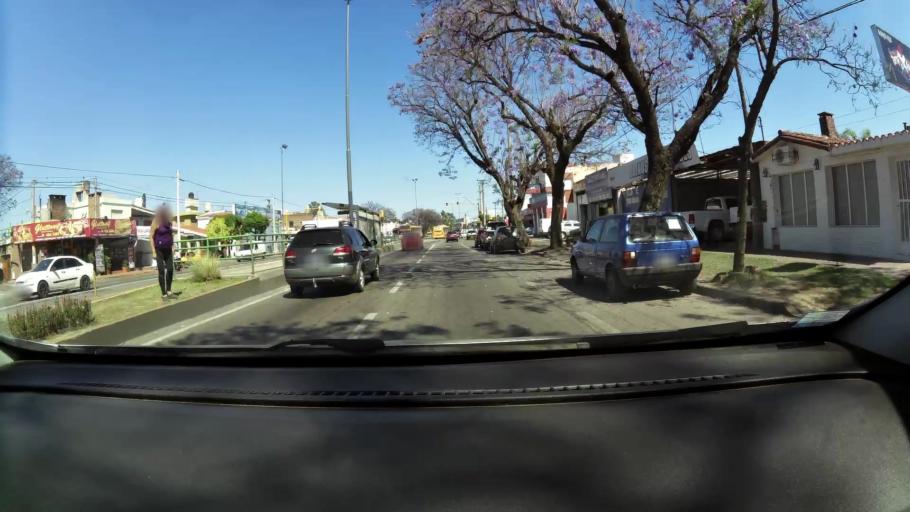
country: AR
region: Cordoba
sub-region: Departamento de Capital
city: Cordoba
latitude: -31.4324
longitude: -64.1362
